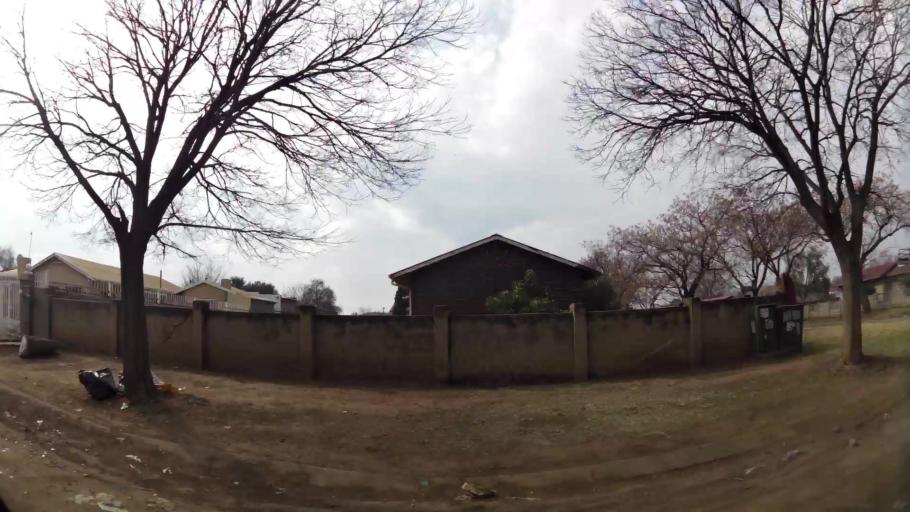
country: ZA
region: Gauteng
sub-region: Sedibeng District Municipality
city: Vanderbijlpark
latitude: -26.6878
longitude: 27.8360
